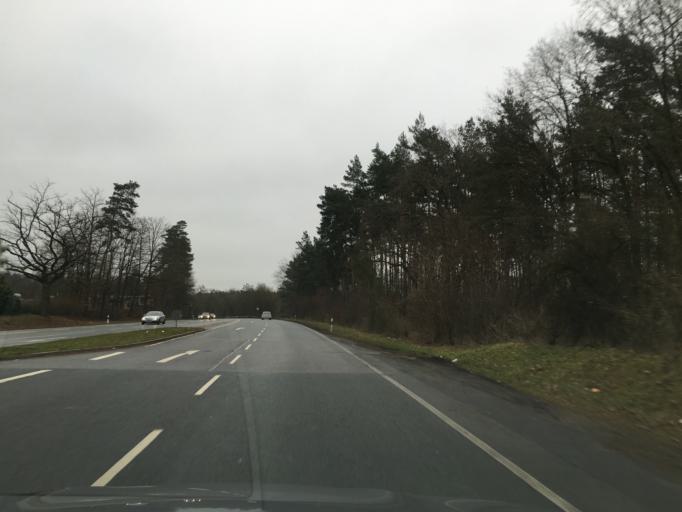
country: DE
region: Bavaria
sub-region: Regierungsbezirk Mittelfranken
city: Neunkirchen am Sand
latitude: 49.5164
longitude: 11.3122
